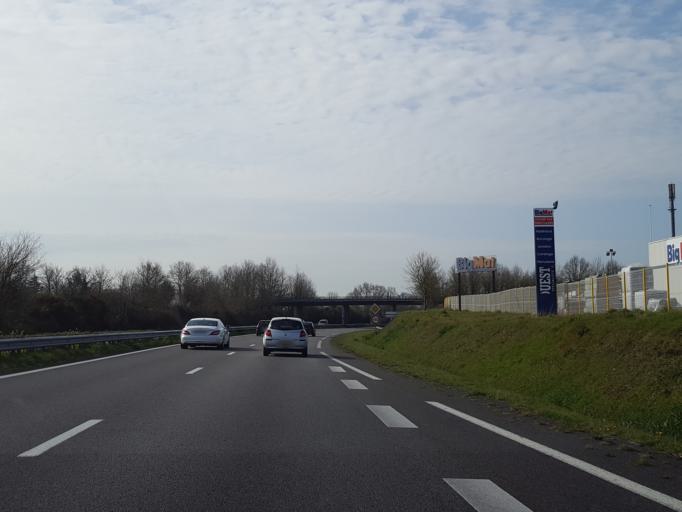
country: FR
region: Pays de la Loire
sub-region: Departement de la Vendee
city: Belleville-sur-Vie
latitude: 46.7801
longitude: -1.4201
